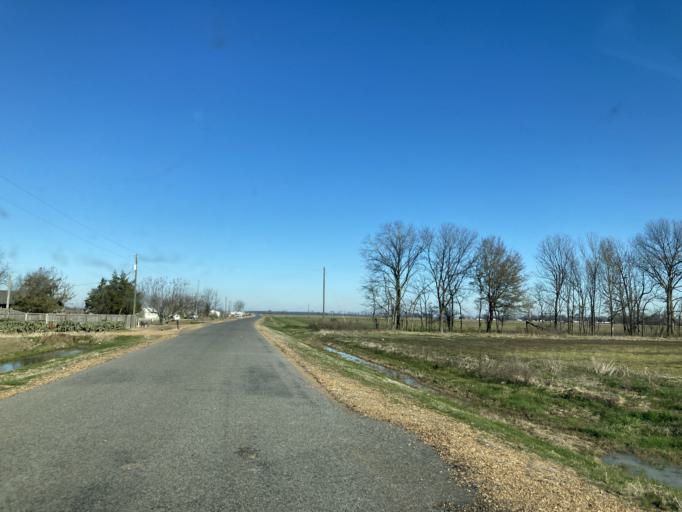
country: US
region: Mississippi
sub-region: Yazoo County
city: Yazoo City
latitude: 32.9628
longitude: -90.6056
